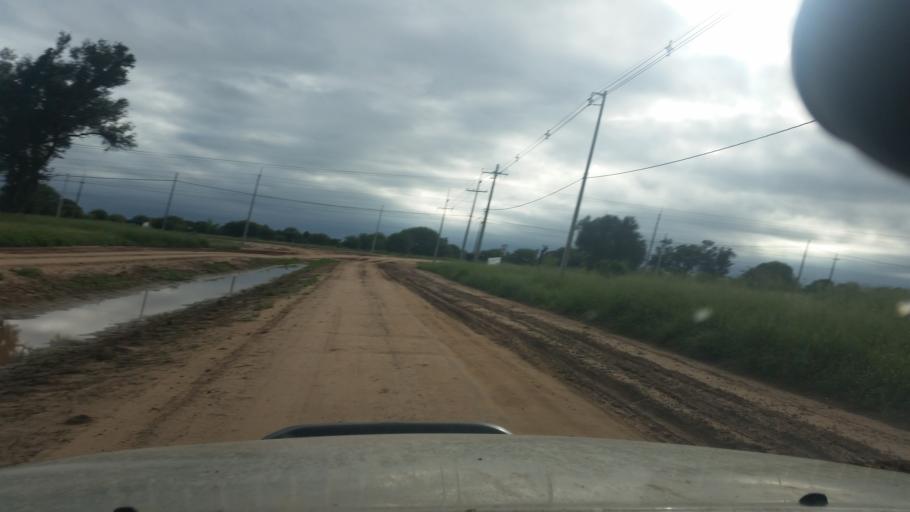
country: PY
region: Boqueron
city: Filadelfia
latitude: -22.3915
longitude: -60.0339
